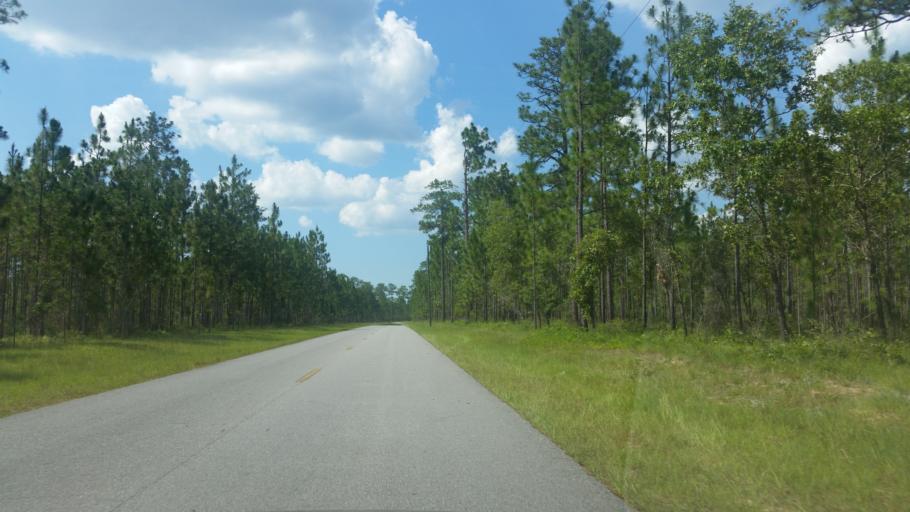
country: US
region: Florida
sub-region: Santa Rosa County
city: East Milton
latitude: 30.6880
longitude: -86.8761
